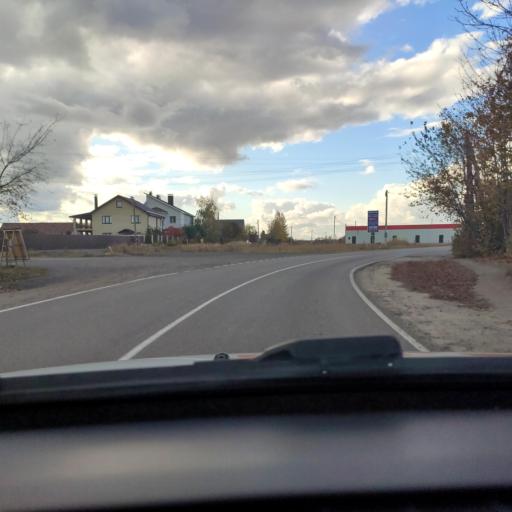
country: RU
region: Voronezj
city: Ramon'
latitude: 51.8253
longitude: 39.2581
